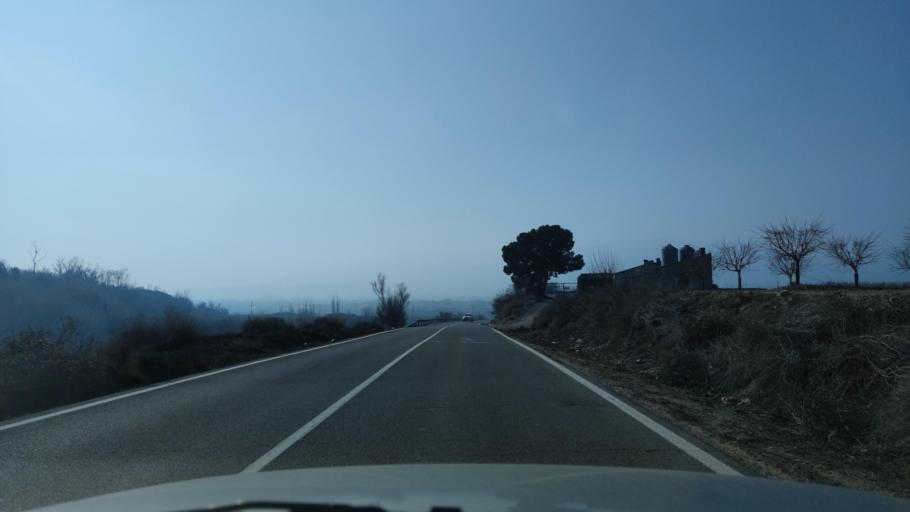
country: ES
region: Catalonia
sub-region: Provincia de Lleida
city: la Granja d'Escarp
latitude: 41.4622
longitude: 0.3680
